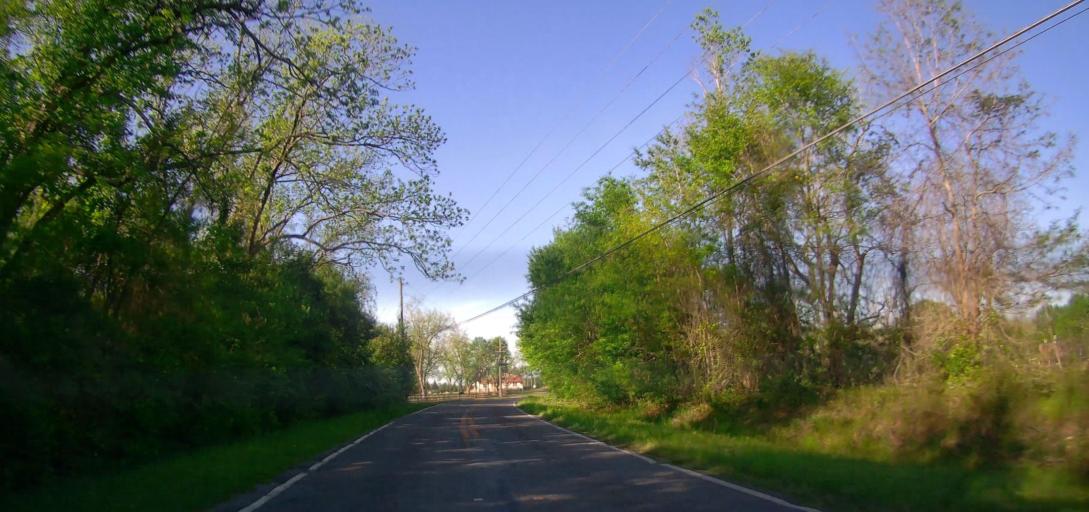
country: US
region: Georgia
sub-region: Houston County
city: Perry
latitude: 32.4805
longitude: -83.8050
